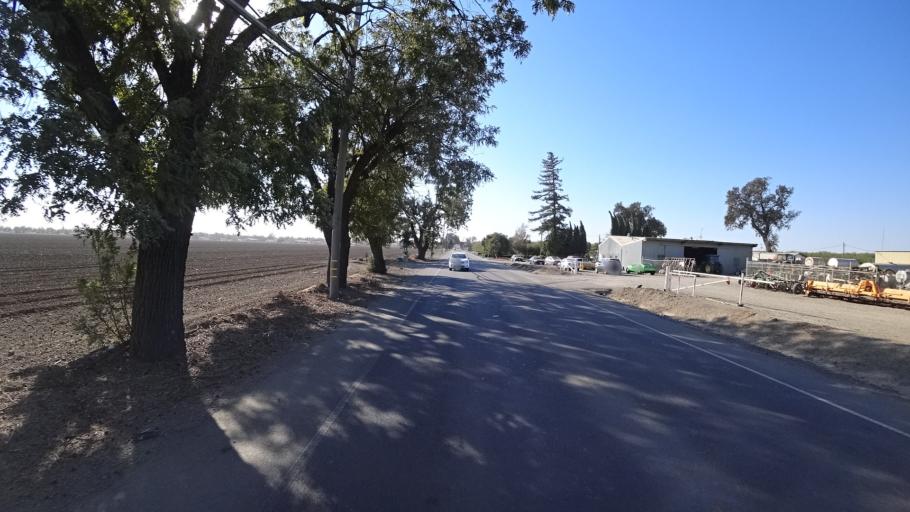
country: US
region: California
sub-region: Yolo County
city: Woodland
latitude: 38.6983
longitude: -121.7839
